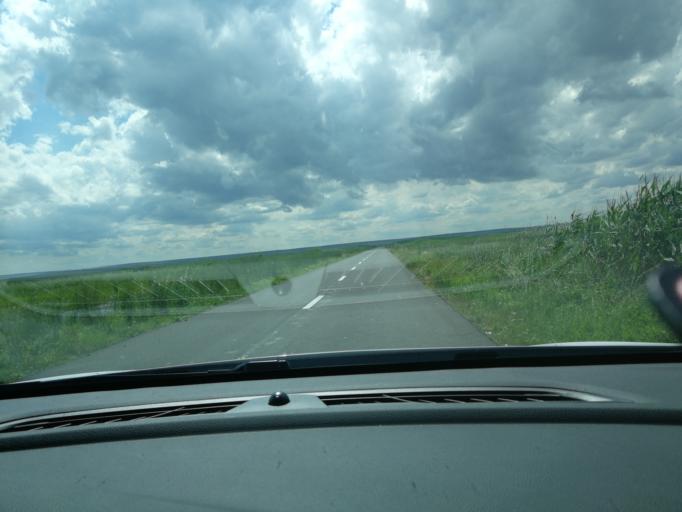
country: RO
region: Constanta
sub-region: Comuna Istria
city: Istria
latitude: 44.5372
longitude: 28.7449
